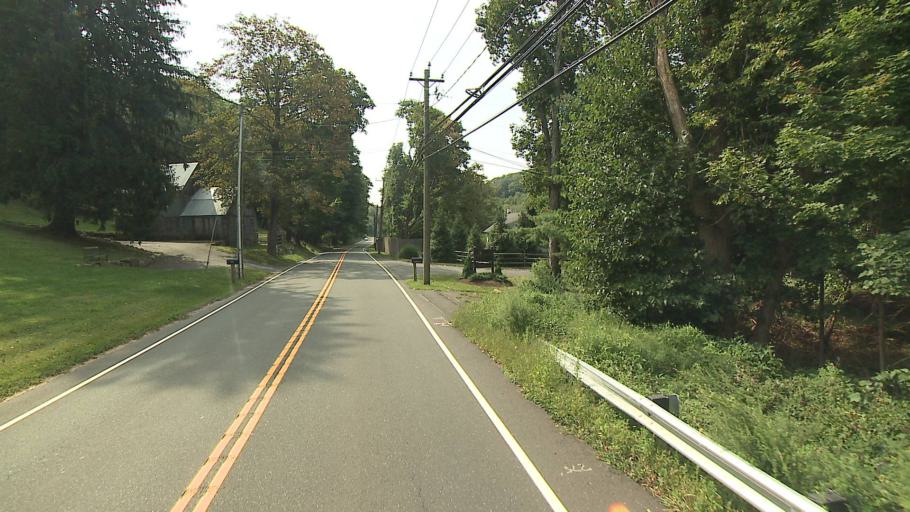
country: US
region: Connecticut
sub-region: Fairfield County
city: Georgetown
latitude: 41.2662
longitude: -73.4256
